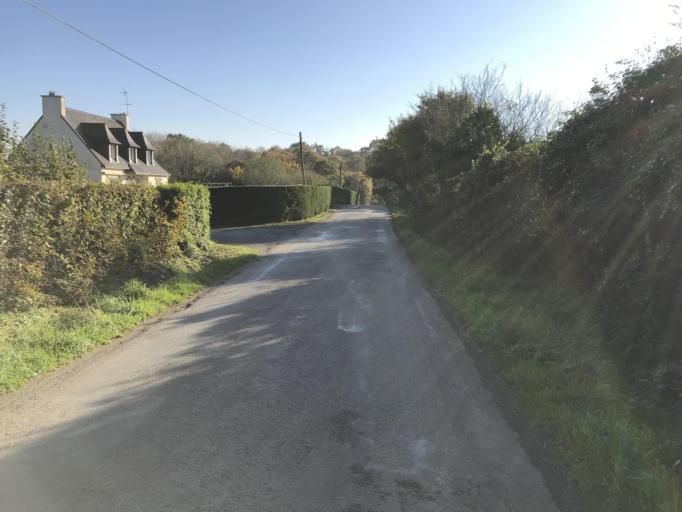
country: FR
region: Brittany
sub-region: Departement du Finistere
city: Hopital-Camfrout
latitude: 48.3210
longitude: -4.2339
